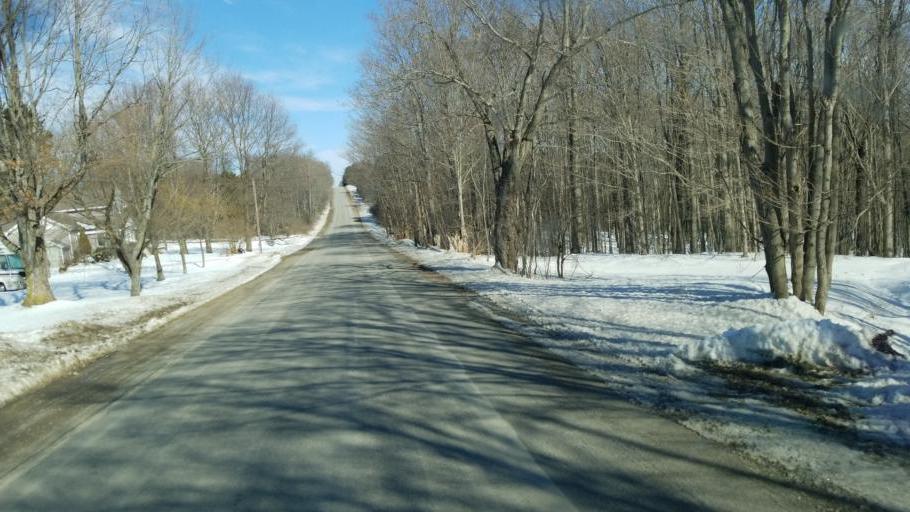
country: US
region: New York
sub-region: Allegany County
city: Andover
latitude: 42.1328
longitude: -77.7581
